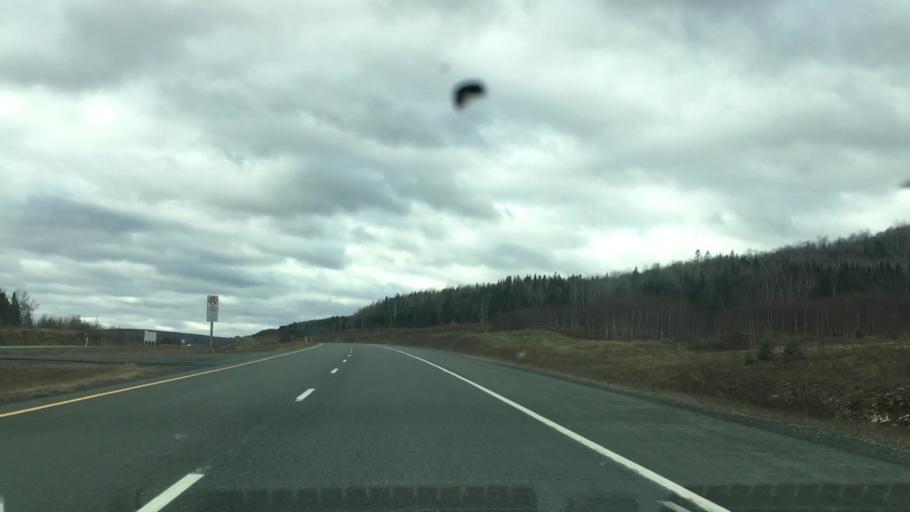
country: US
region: Maine
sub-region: Aroostook County
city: Fort Fairfield
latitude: 46.7272
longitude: -67.7273
